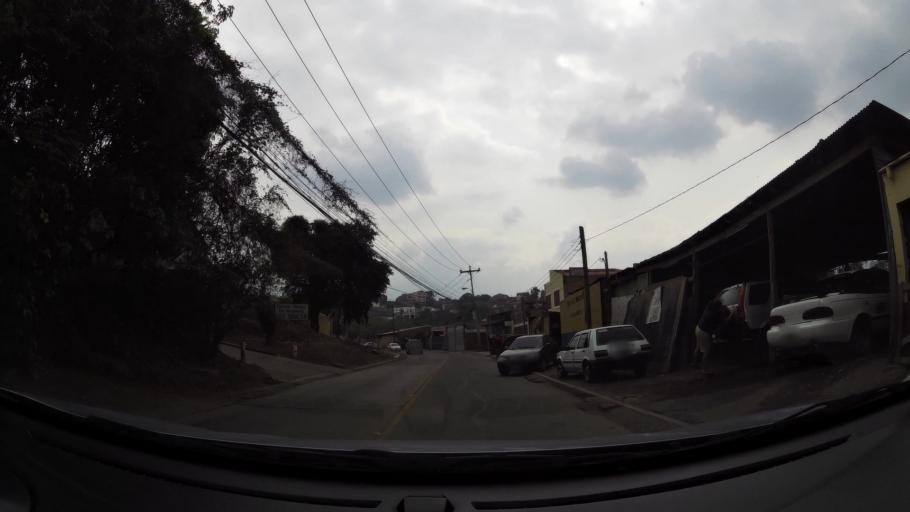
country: HN
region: Francisco Morazan
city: Tegucigalpa
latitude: 14.0903
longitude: -87.1724
